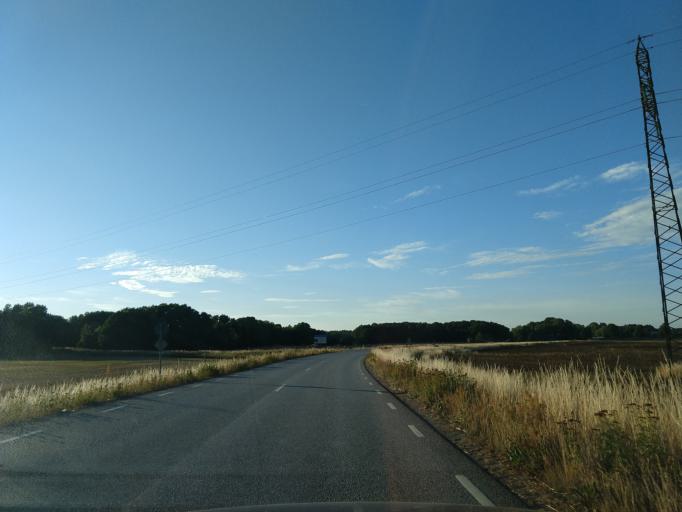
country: SE
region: Blekinge
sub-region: Ronneby Kommun
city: Brakne-Hoby
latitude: 56.2459
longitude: 15.1156
